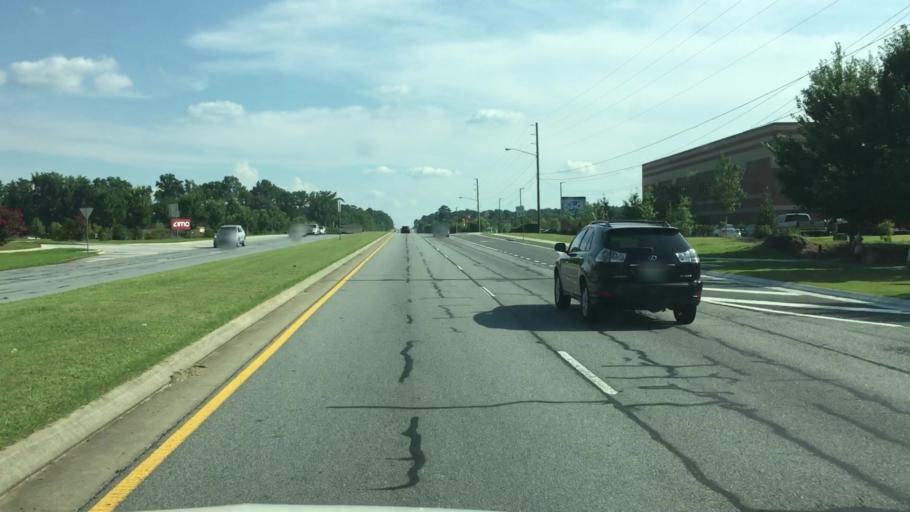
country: US
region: Georgia
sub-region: Gwinnett County
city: Grayson
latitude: 33.9053
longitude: -84.0039
